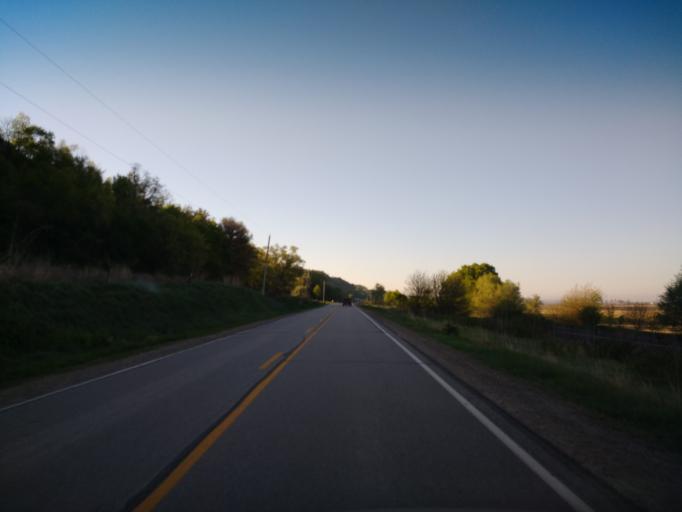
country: US
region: Iowa
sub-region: Harrison County
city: Missouri Valley
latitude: 41.4866
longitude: -95.8867
